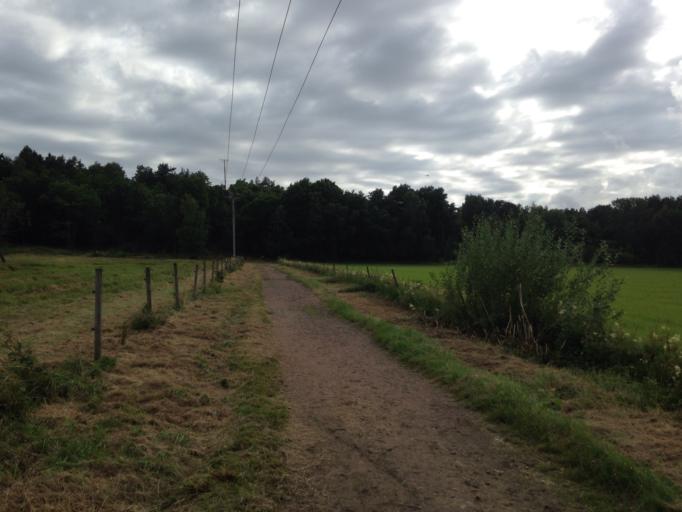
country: SE
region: Vaestra Goetaland
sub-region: Kungalvs Kommun
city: Kungalv
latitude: 57.8174
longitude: 11.8894
